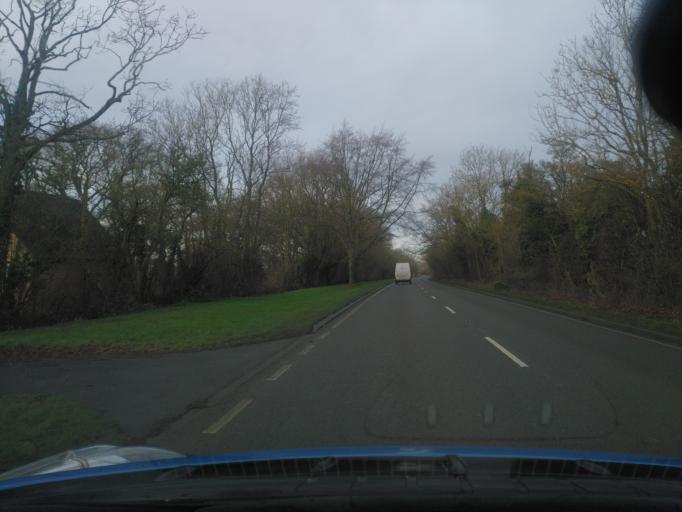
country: GB
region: England
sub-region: Gloucestershire
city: Moreton in Marsh
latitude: 51.9824
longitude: -1.6531
